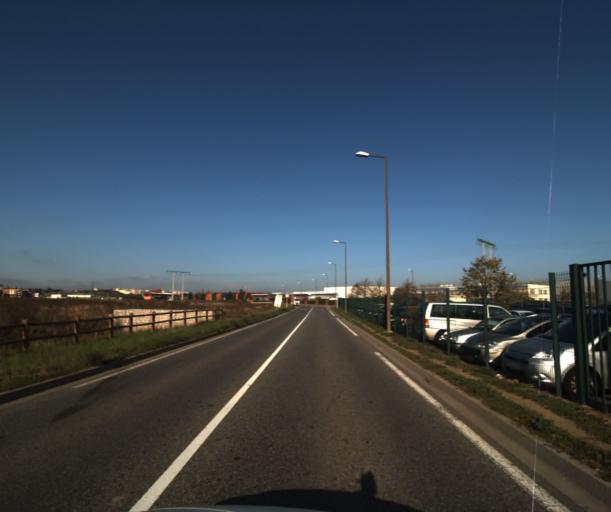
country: FR
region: Midi-Pyrenees
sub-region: Departement de la Haute-Garonne
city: Colomiers
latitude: 43.5987
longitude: 1.3619
